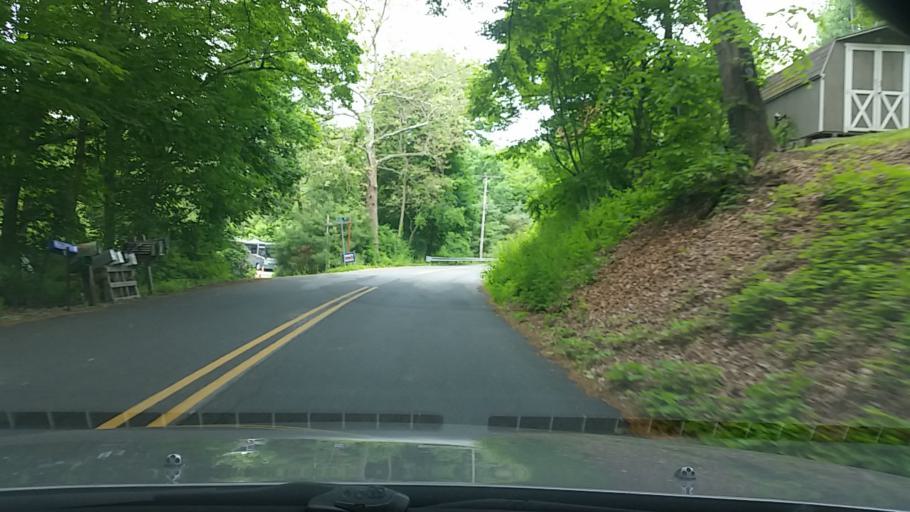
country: US
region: New Jersey
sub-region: Warren County
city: Oxford
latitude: 40.8606
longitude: -74.9787
